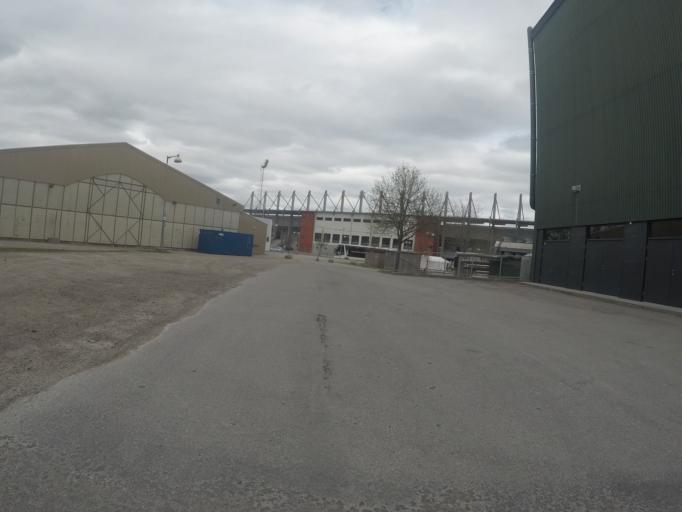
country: SE
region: Vaestmanland
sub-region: Vasteras
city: Vasteras
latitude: 59.6266
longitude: 16.5279
